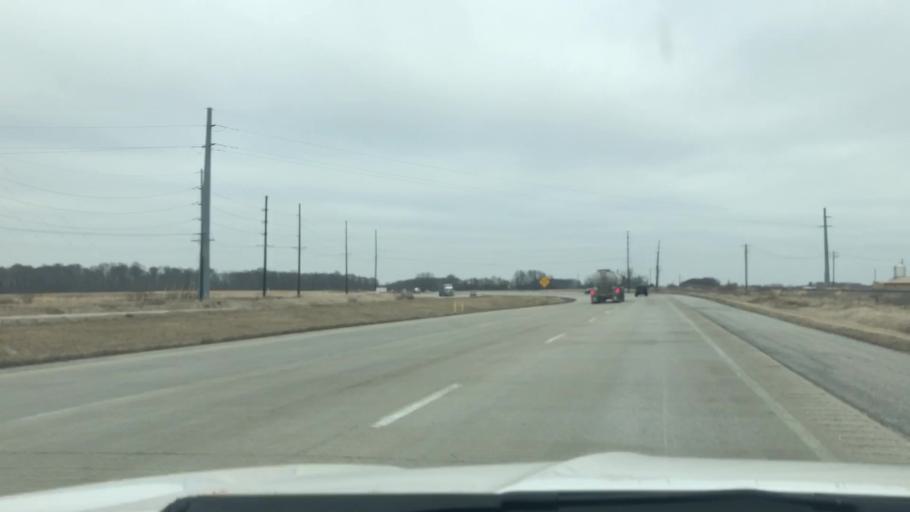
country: US
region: Indiana
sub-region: Cass County
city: Dunkirk
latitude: 40.7204
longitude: -86.4240
